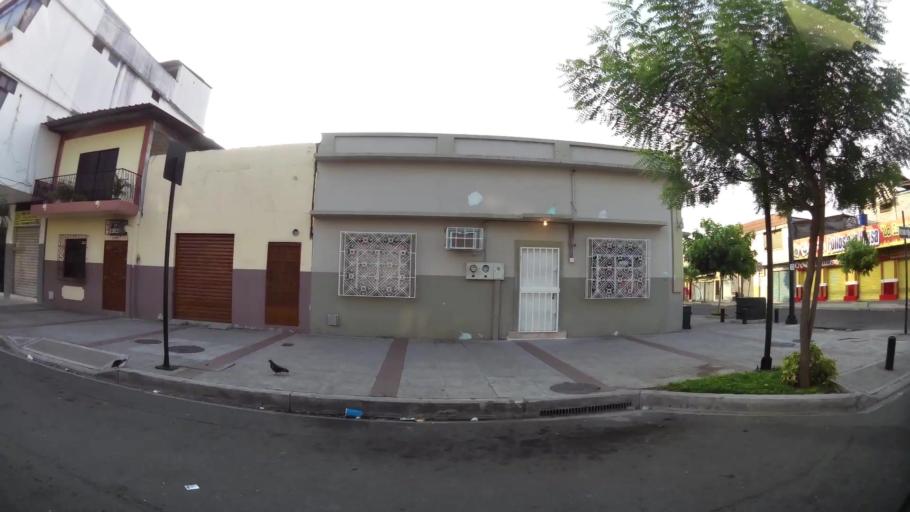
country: EC
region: Guayas
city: Guayaquil
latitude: -2.2107
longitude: -79.9010
